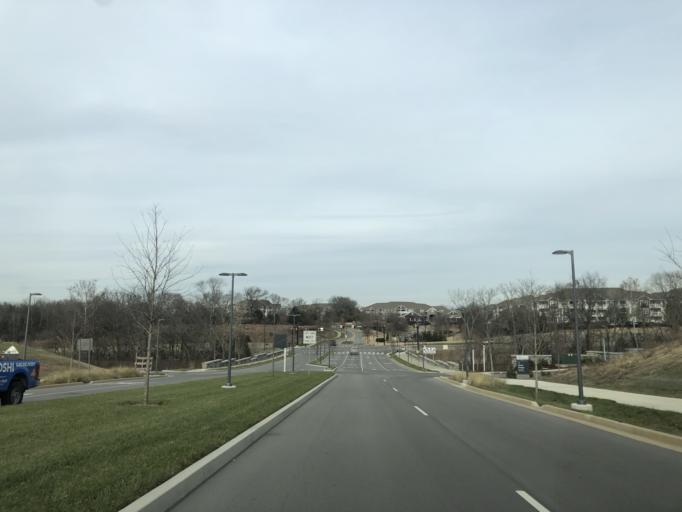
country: US
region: Tennessee
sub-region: Williamson County
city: Franklin
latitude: 35.9307
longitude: -86.8061
